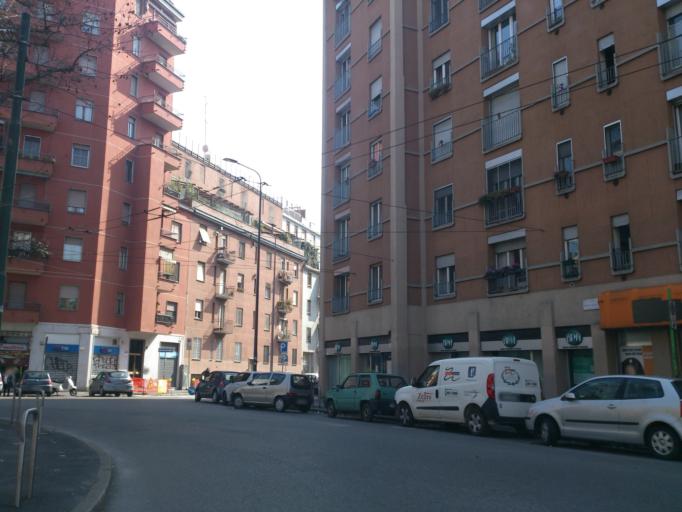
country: IT
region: Lombardy
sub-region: Citta metropolitana di Milano
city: Milano
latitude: 45.4501
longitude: 9.2204
